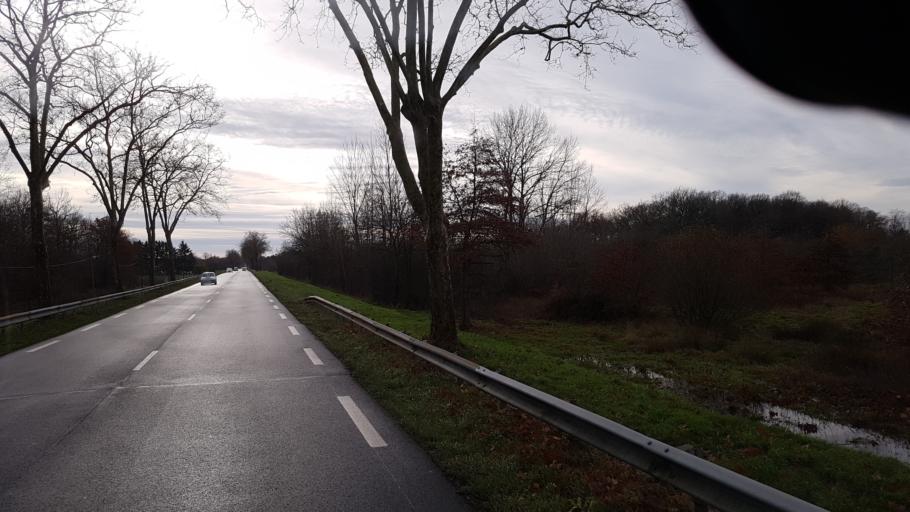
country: FR
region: Centre
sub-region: Departement du Loiret
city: Saint-Cyr-en-Val
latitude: 47.7951
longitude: 1.9324
